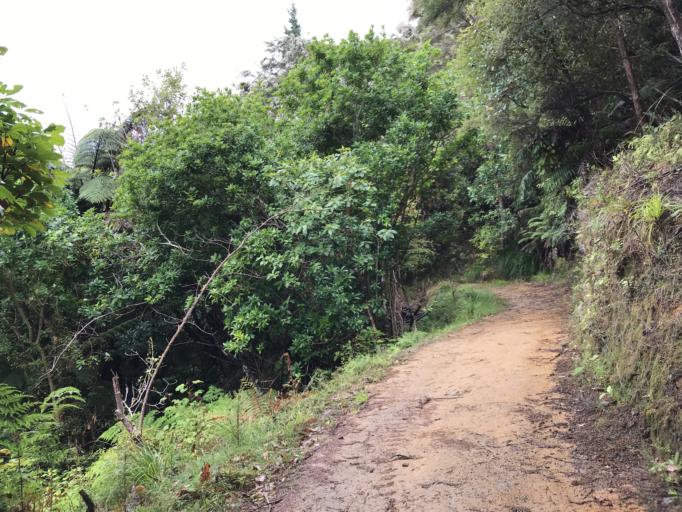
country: NZ
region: Marlborough
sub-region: Marlborough District
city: Picton
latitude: -41.1142
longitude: 174.1640
